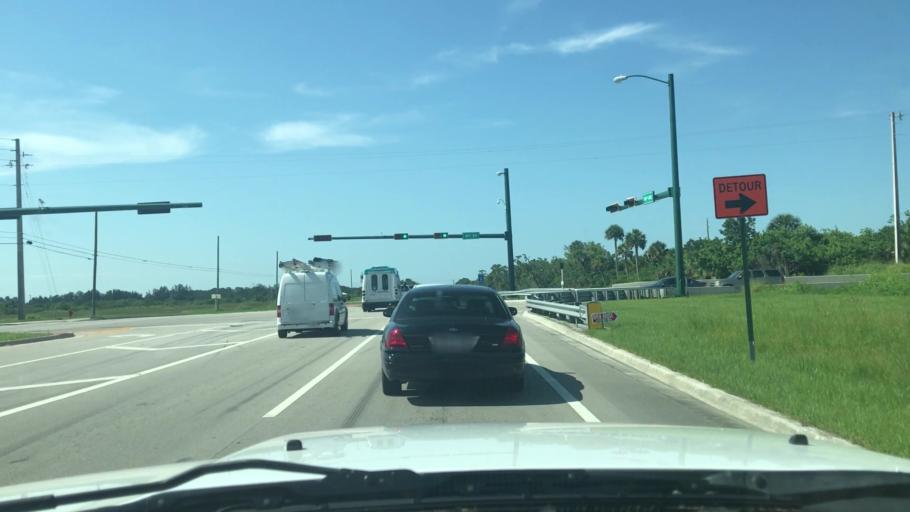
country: US
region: Florida
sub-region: Indian River County
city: West Vero Corridor
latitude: 27.6676
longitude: -80.4630
